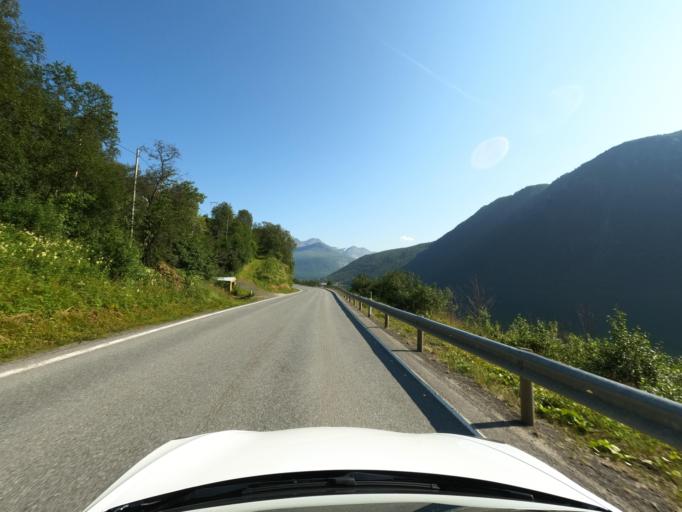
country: NO
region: Nordland
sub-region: Narvik
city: Narvik
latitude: 68.3891
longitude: 17.5492
